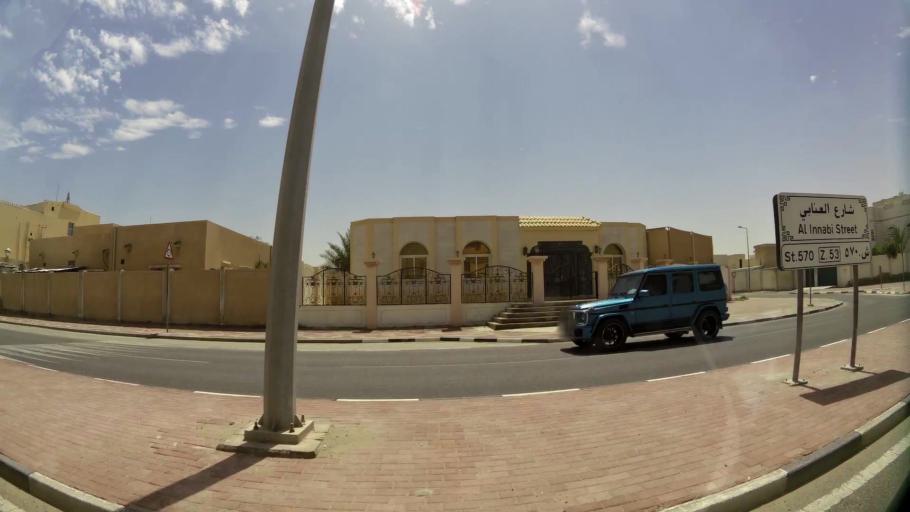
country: QA
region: Baladiyat ar Rayyan
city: Ar Rayyan
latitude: 25.2997
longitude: 51.4104
